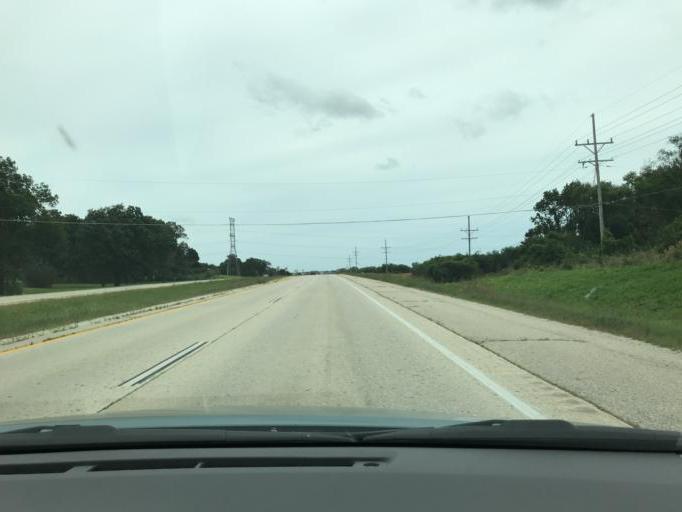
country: US
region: Wisconsin
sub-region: Kenosha County
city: Pleasant Prairie
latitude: 42.5672
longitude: -87.9724
